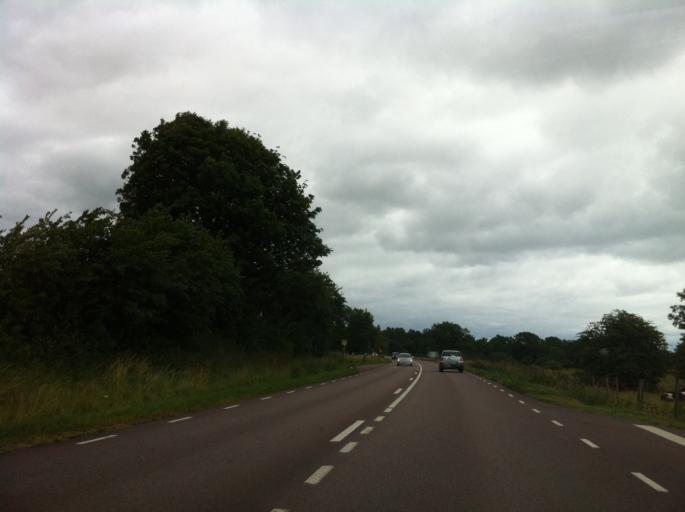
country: SE
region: Kalmar
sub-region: Borgholms Kommun
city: Borgholm
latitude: 57.1729
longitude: 17.0255
